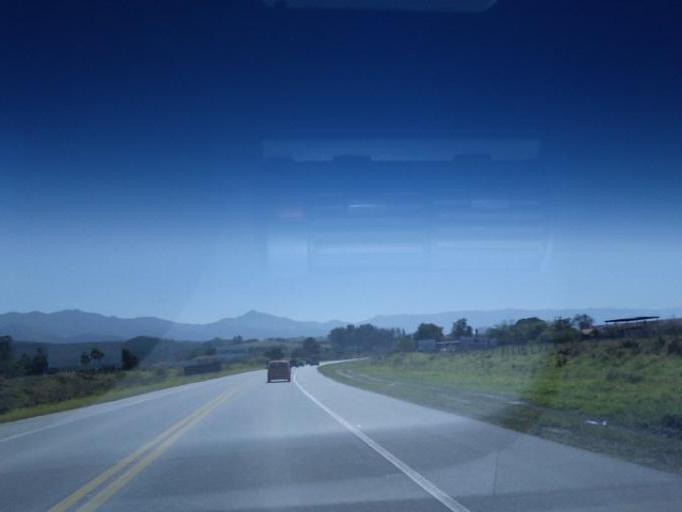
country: BR
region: Sao Paulo
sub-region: Tremembe
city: Tremembe
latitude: -22.9838
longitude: -45.6481
